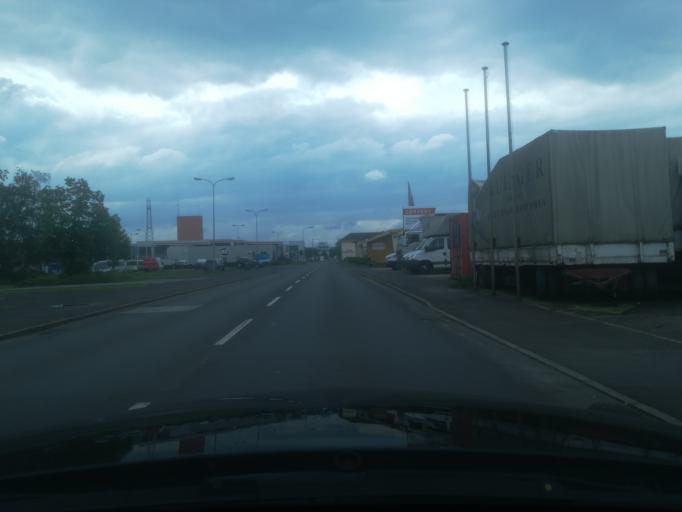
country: AT
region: Upper Austria
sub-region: Politischer Bezirk Urfahr-Umgebung
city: Steyregg
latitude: 48.2728
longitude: 14.3236
